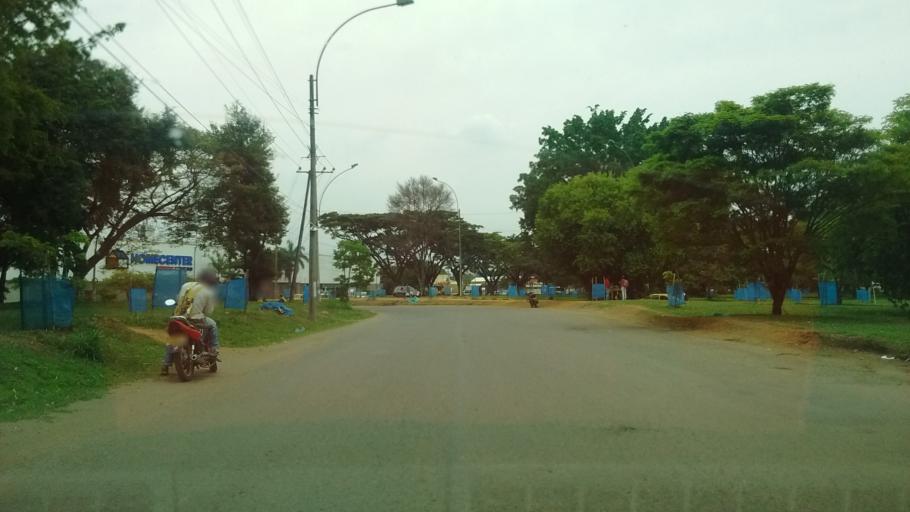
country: CO
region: Valle del Cauca
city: Cali
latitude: 3.3668
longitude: -76.5252
